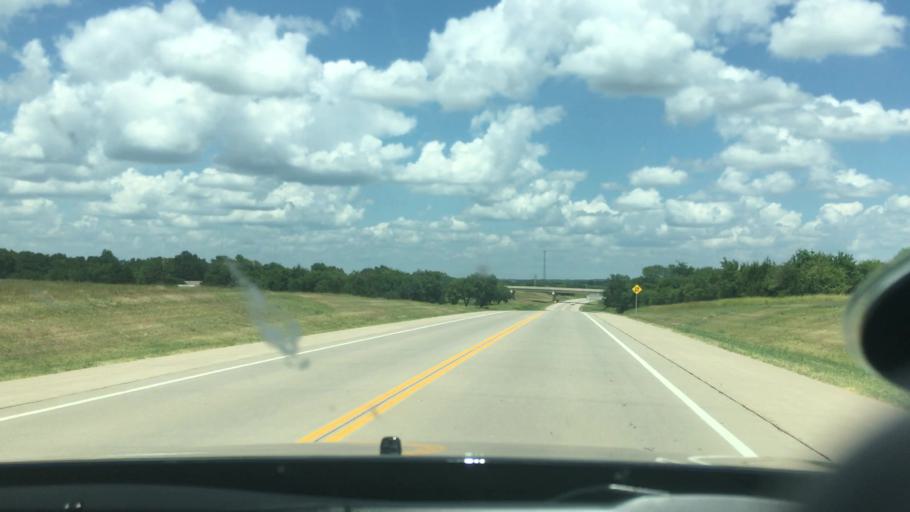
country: US
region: Oklahoma
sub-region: Murray County
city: Sulphur
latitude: 34.5384
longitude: -96.9888
